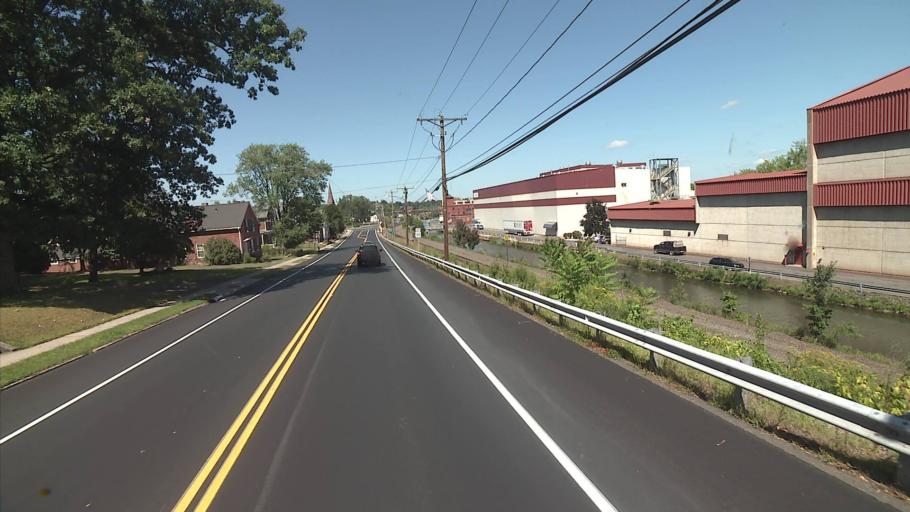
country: US
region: Connecticut
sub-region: Hartford County
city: Windsor Locks
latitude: 41.9226
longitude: -72.6264
